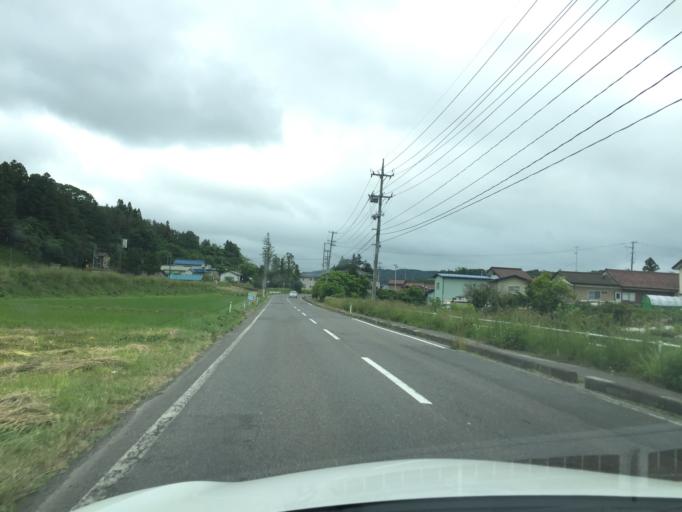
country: JP
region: Fukushima
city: Funehikimachi-funehiki
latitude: 37.4145
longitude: 140.6088
